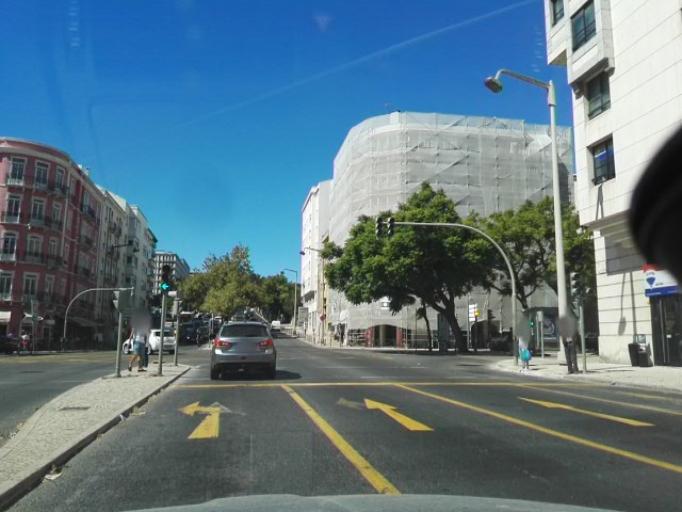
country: PT
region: Lisbon
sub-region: Lisbon
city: Lisbon
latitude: 38.7477
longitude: -9.1499
